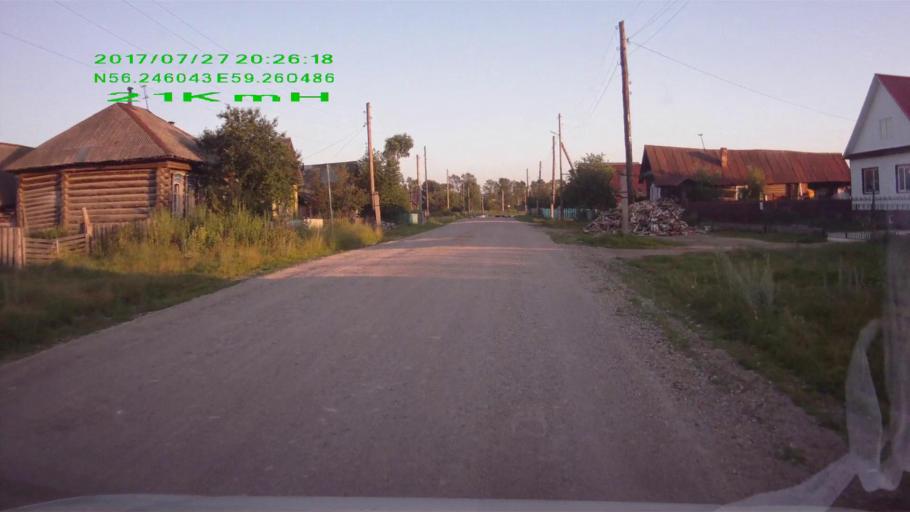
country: RU
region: Sverdlovsk
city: Mikhaylovsk
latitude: 56.2457
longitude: 59.2599
